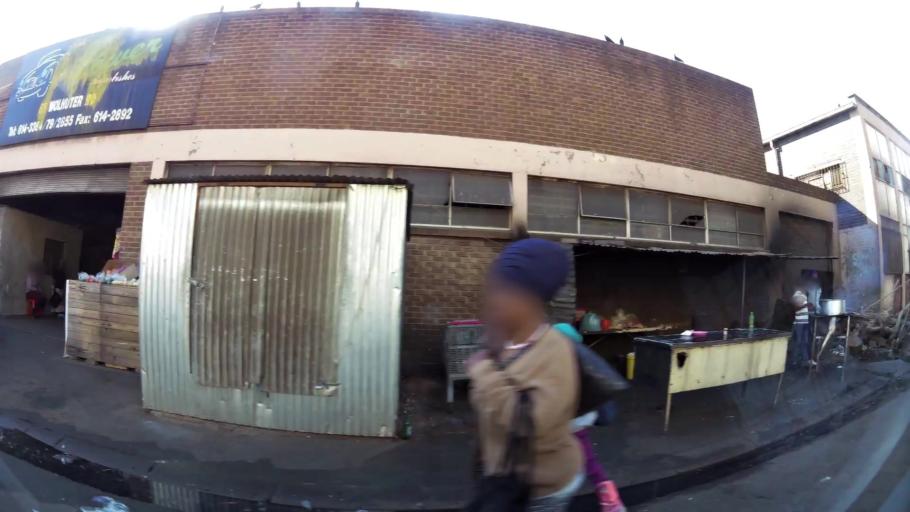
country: ZA
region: Gauteng
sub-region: City of Johannesburg Metropolitan Municipality
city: Johannesburg
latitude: -26.2089
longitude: 28.0683
